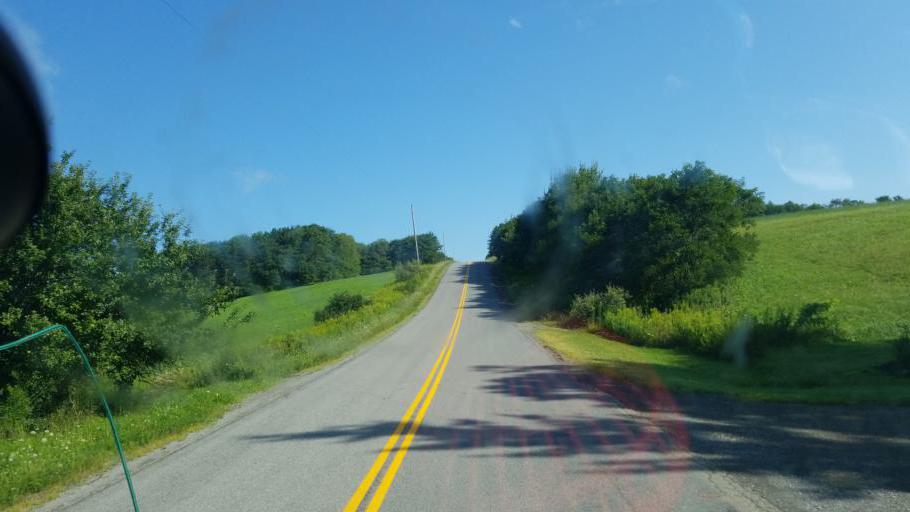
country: US
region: New York
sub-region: Allegany County
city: Andover
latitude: 42.1591
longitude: -77.7133
